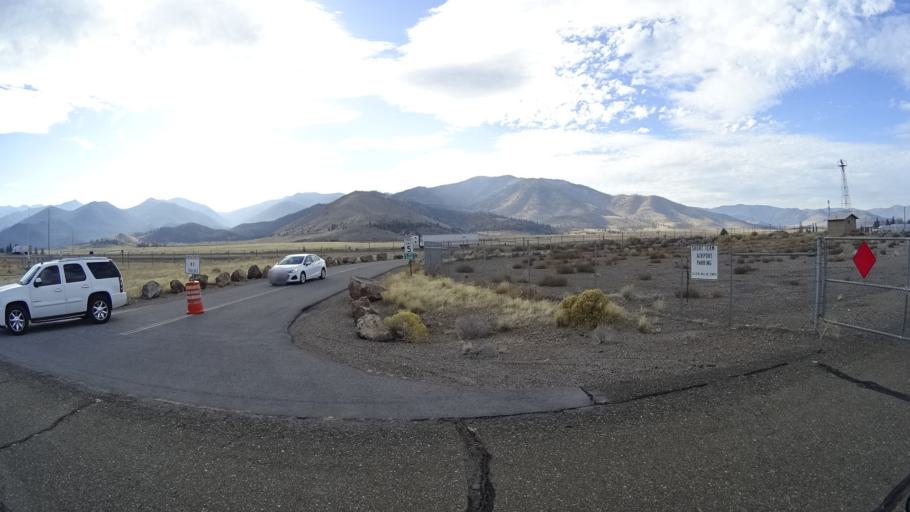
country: US
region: California
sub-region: Siskiyou County
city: Weed
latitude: 41.4759
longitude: -122.4532
